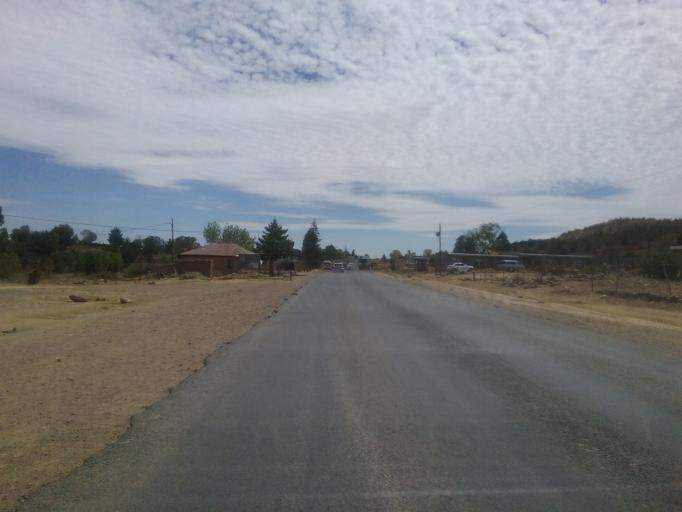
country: LS
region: Mafeteng
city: Mafeteng
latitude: -29.8364
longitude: 27.2328
